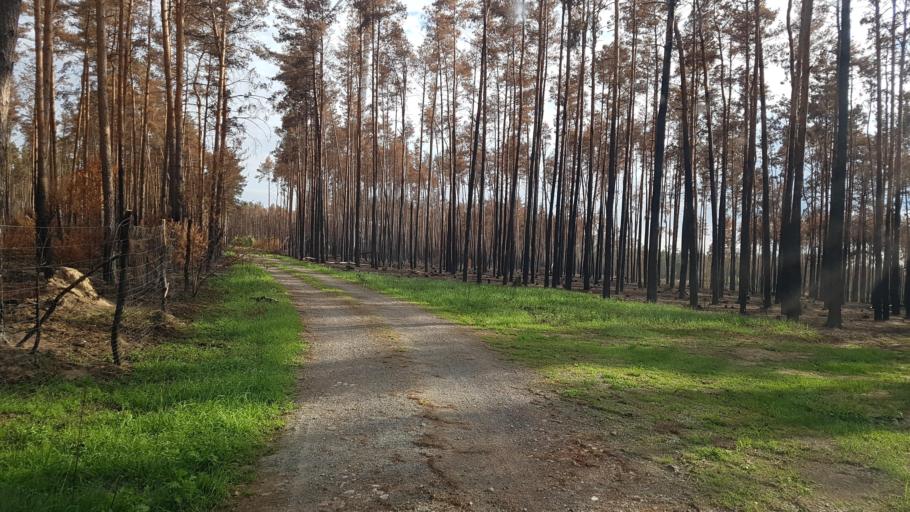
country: DE
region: Saxony
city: Arzberg
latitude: 51.5619
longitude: 13.1789
